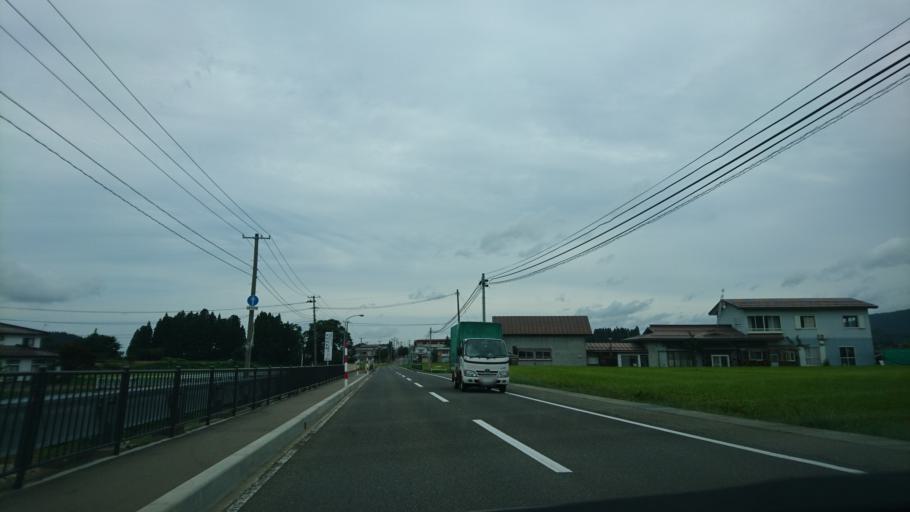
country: JP
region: Akita
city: Yuzawa
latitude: 39.1725
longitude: 140.5569
